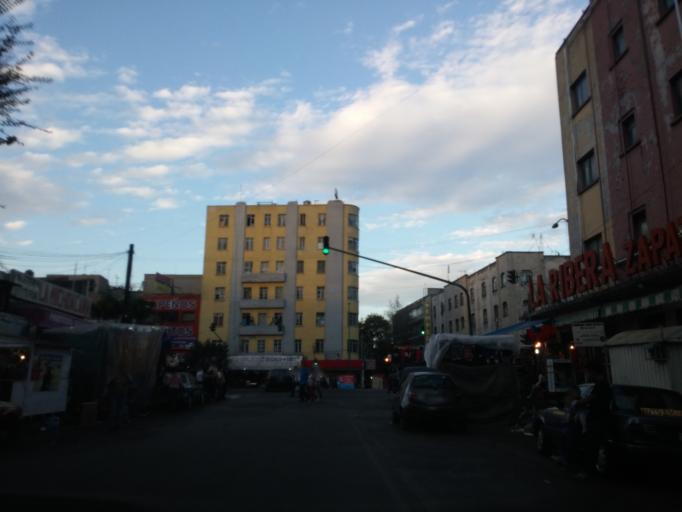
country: MX
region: Mexico City
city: Cuauhtemoc
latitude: 19.4407
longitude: -99.1587
